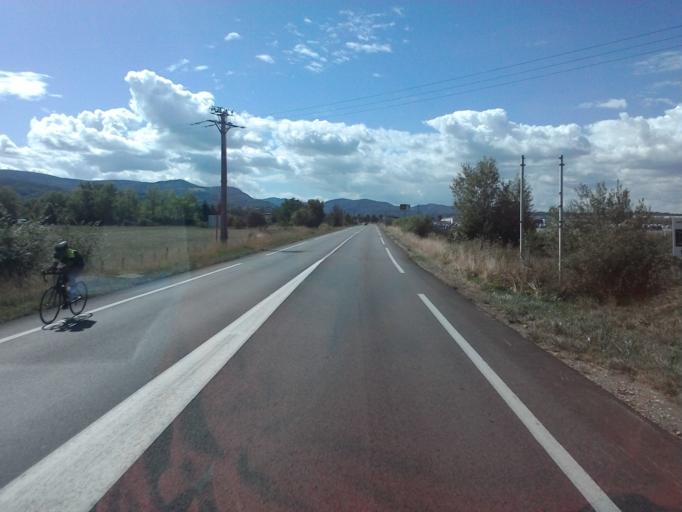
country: FR
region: Rhone-Alpes
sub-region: Departement de l'Ain
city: Ambronay
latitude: 45.9882
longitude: 5.3447
